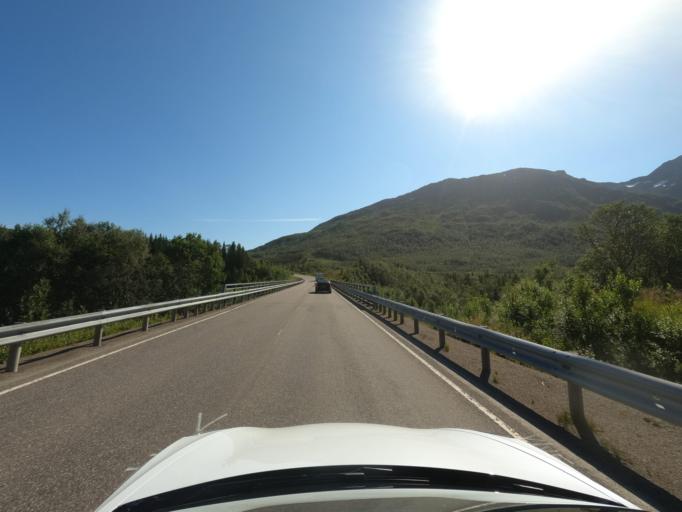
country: NO
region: Nordland
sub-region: Lodingen
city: Lodingen
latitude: 68.5292
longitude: 15.7507
